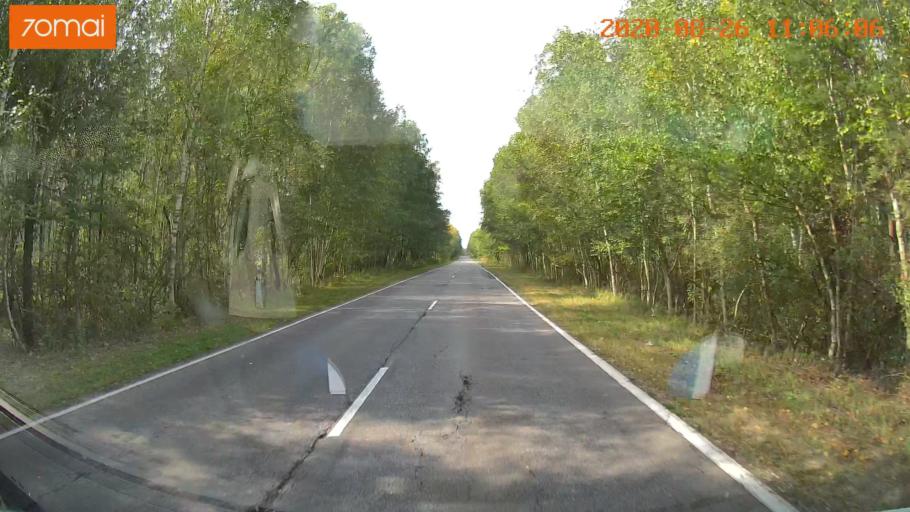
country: RU
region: Rjazan
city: Izhevskoye
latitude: 54.5242
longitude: 41.1562
